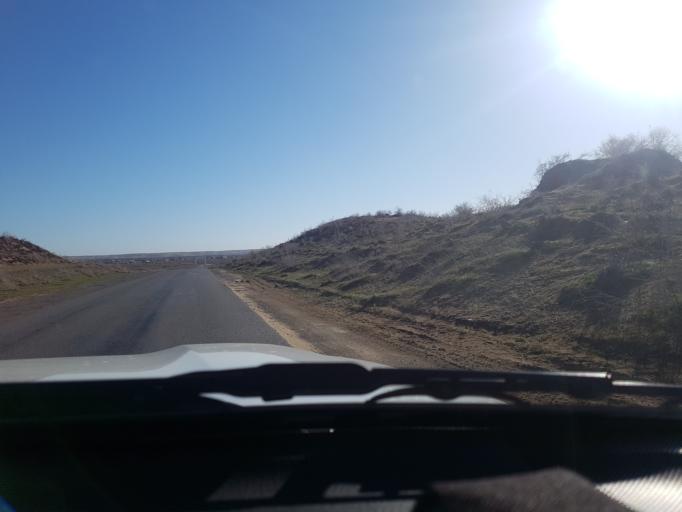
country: TM
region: Mary
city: Yoloeten
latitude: 37.0376
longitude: 62.4472
